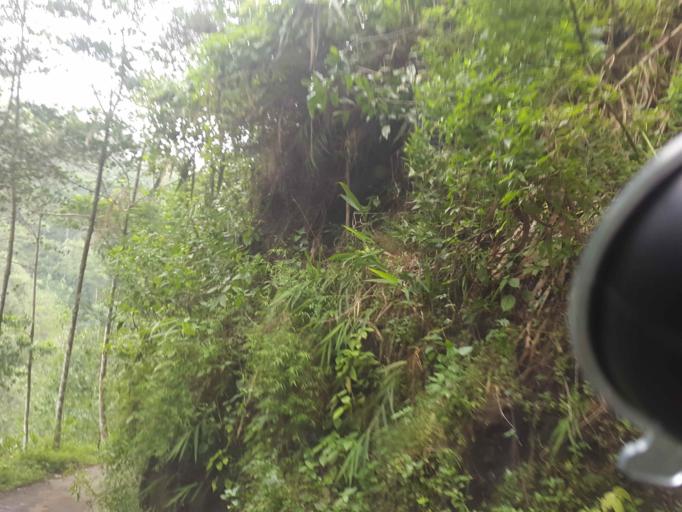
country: ID
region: Central Java
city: Gombong
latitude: -7.5629
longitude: 109.4082
